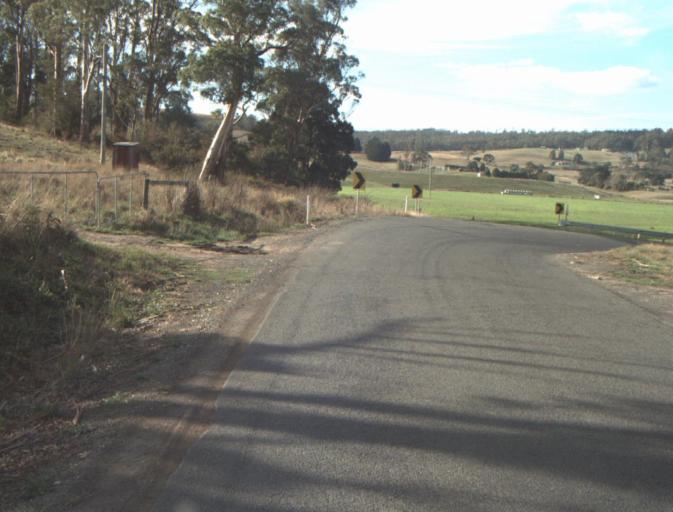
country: AU
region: Tasmania
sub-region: Launceston
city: Mayfield
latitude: -41.2367
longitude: 147.1972
